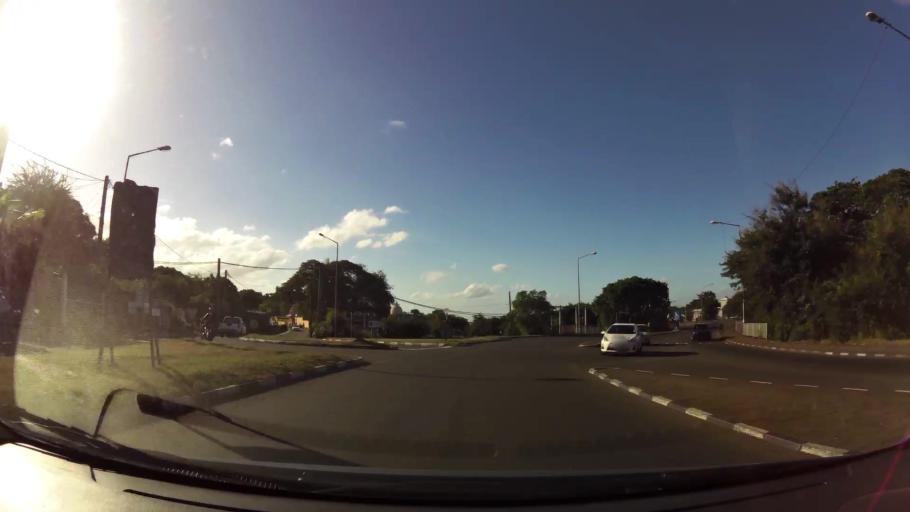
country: MU
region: Moka
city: Pailles
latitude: -20.1758
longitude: 57.4711
